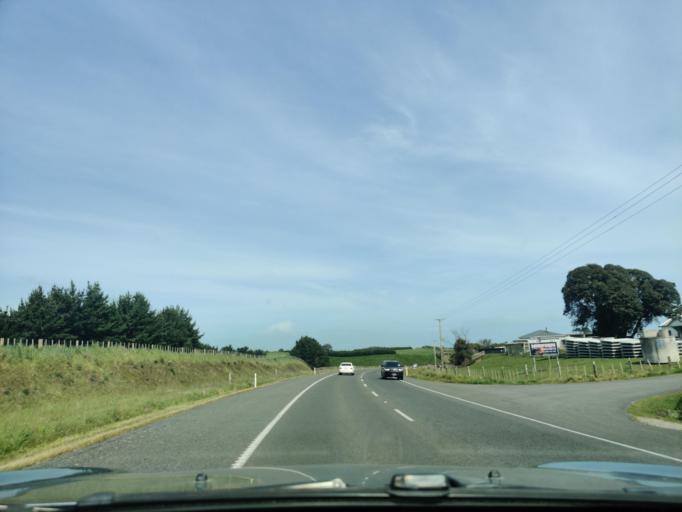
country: NZ
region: Taranaki
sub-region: South Taranaki District
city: Patea
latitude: -39.6677
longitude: 174.4031
